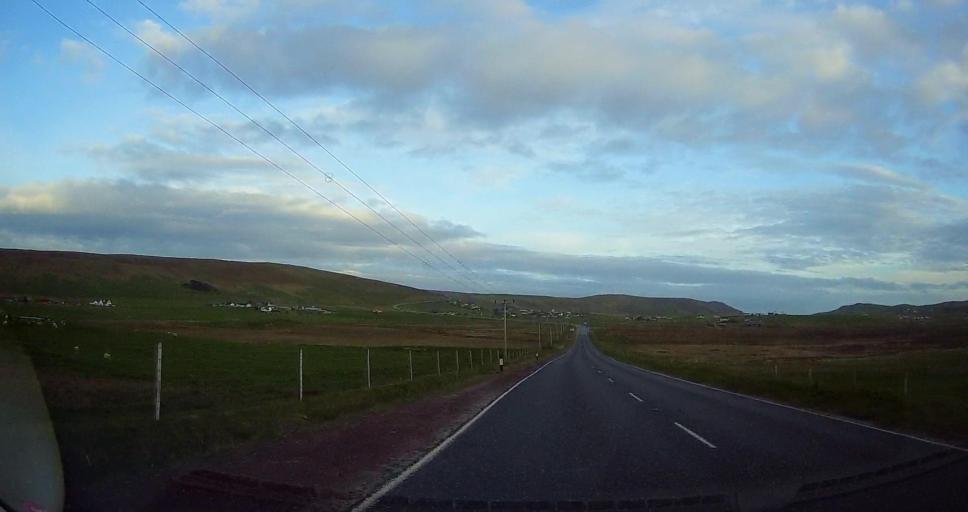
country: GB
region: Scotland
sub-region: Shetland Islands
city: Lerwick
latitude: 60.1973
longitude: -1.2321
